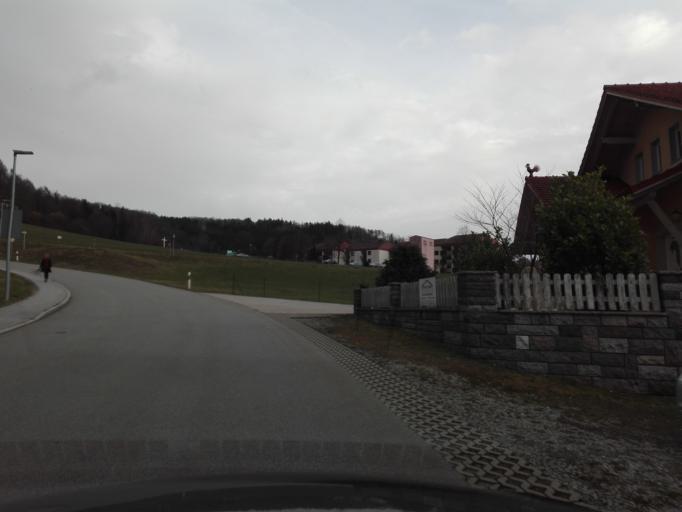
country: DE
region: Bavaria
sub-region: Lower Bavaria
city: Obernzell
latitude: 48.5583
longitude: 13.6354
